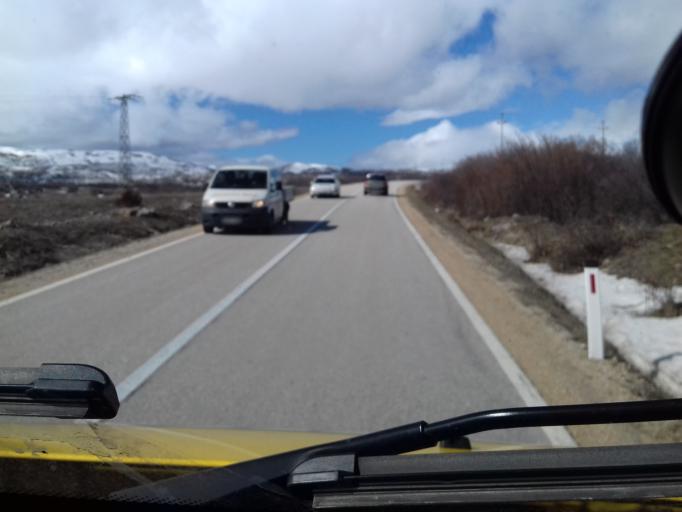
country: BA
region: Federation of Bosnia and Herzegovina
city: Tomislavgrad
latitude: 43.7748
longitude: 17.2309
